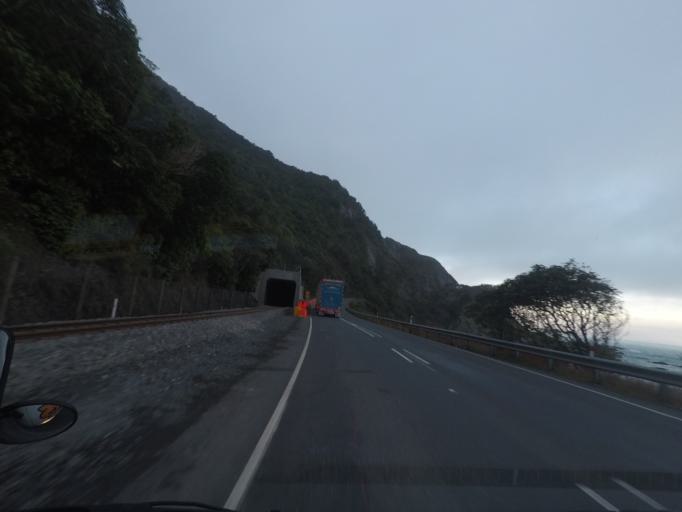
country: NZ
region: Canterbury
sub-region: Kaikoura District
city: Kaikoura
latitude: -42.4502
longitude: 173.5726
